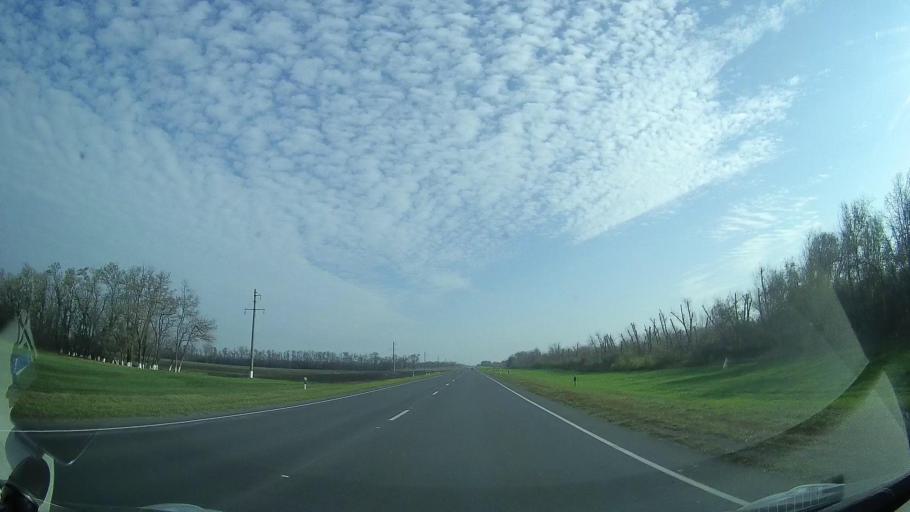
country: RU
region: Rostov
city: Gigant
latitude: 46.5271
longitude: 41.2162
